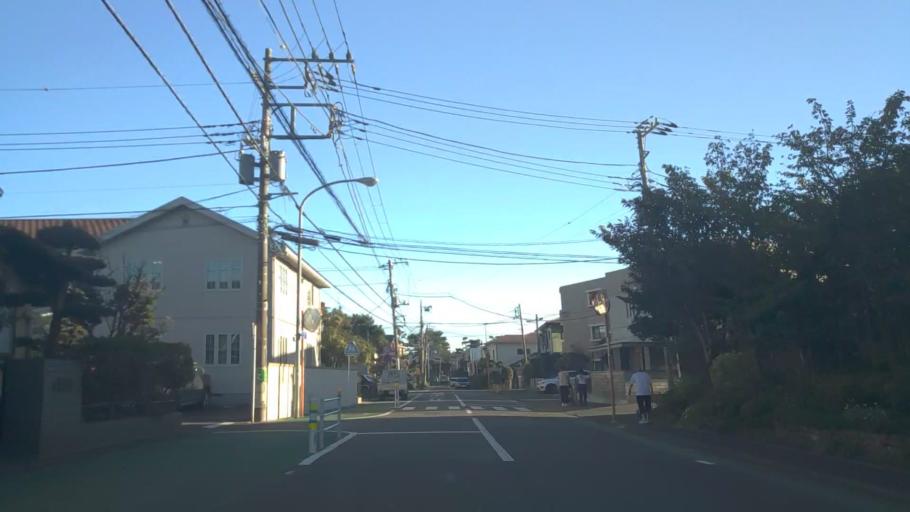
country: JP
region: Kanagawa
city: Chigasaki
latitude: 35.3238
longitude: 139.4151
